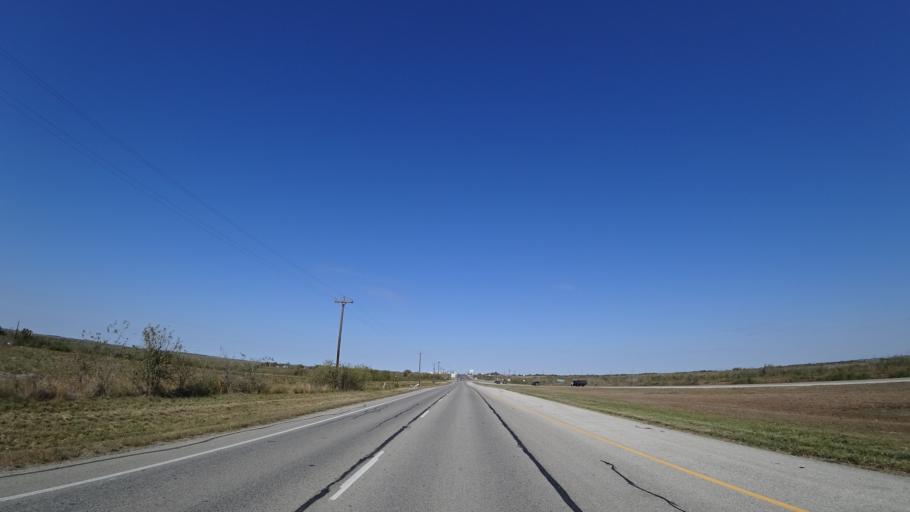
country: US
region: Texas
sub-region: Travis County
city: Onion Creek
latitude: 30.0862
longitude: -97.6935
